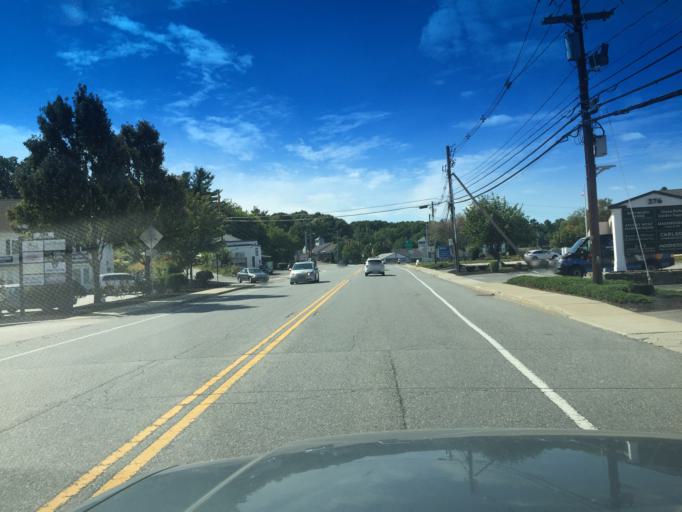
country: US
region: Massachusetts
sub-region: Worcester County
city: Northborough
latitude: 42.3086
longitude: -71.6567
